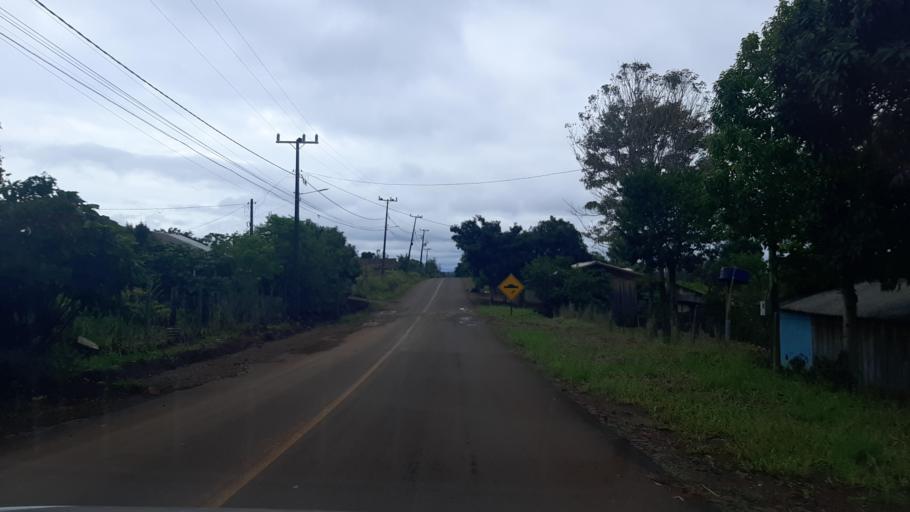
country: BR
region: Parana
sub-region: Ampere
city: Ampere
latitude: -26.0376
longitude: -53.5060
